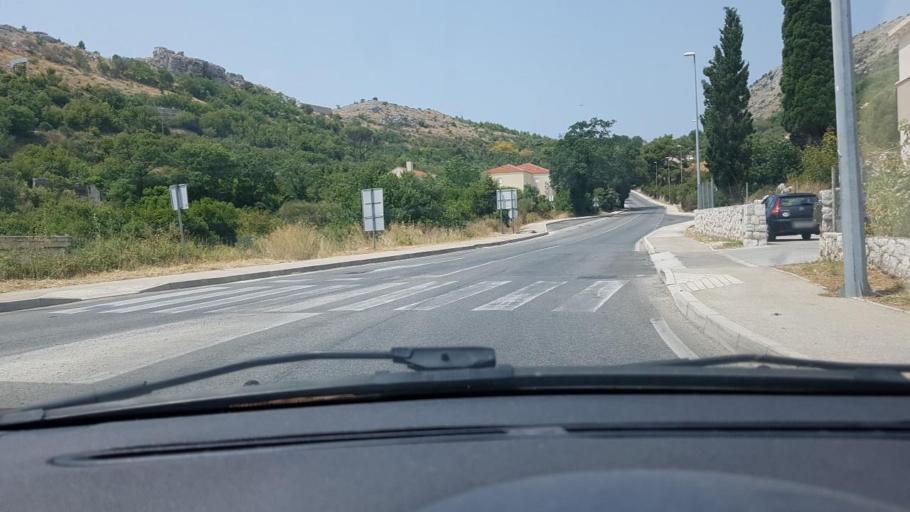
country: HR
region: Dubrovacko-Neretvanska
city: Cibaca
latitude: 42.6305
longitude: 18.1613
